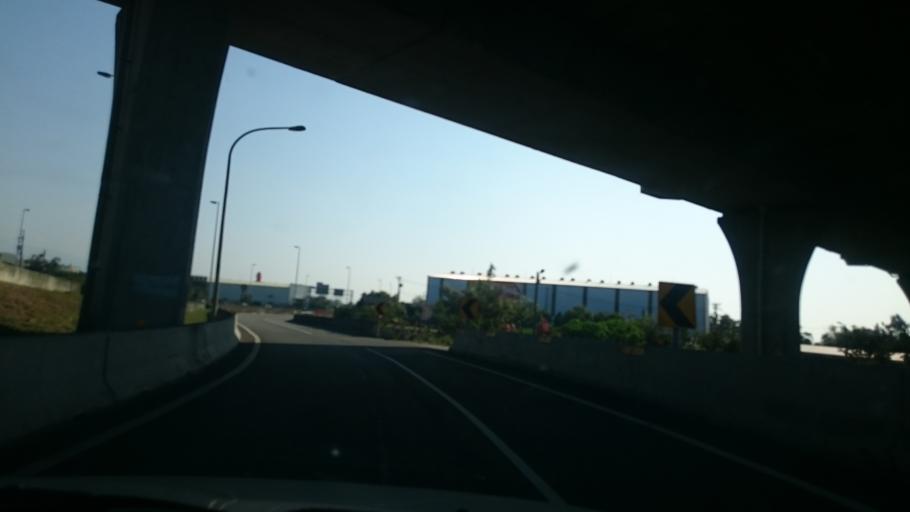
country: TW
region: Taiwan
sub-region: Miaoli
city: Miaoli
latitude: 24.7013
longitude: 120.8657
